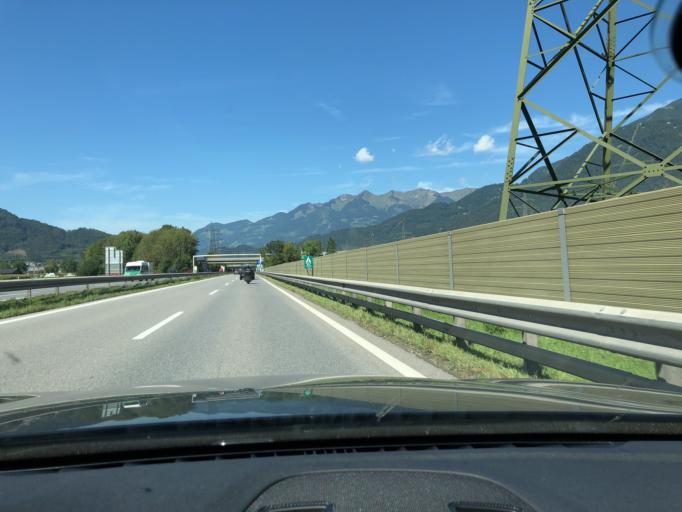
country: AT
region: Vorarlberg
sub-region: Politischer Bezirk Bludenz
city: Bludenz
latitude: 47.1431
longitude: 9.8227
